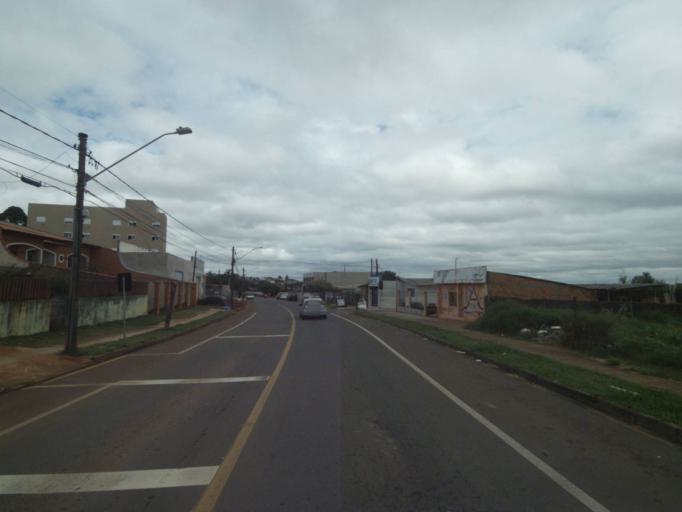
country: BR
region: Parana
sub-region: Telemaco Borba
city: Telemaco Borba
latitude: -24.3329
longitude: -50.6322
